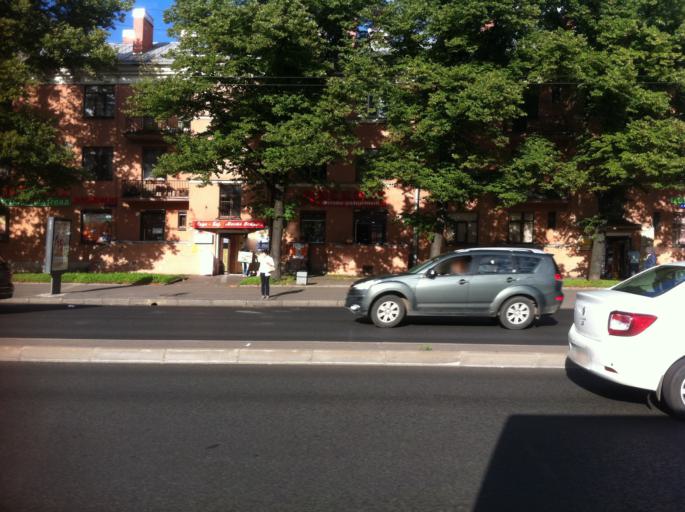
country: RU
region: St.-Petersburg
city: Admiralteisky
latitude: 59.8986
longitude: 30.2755
